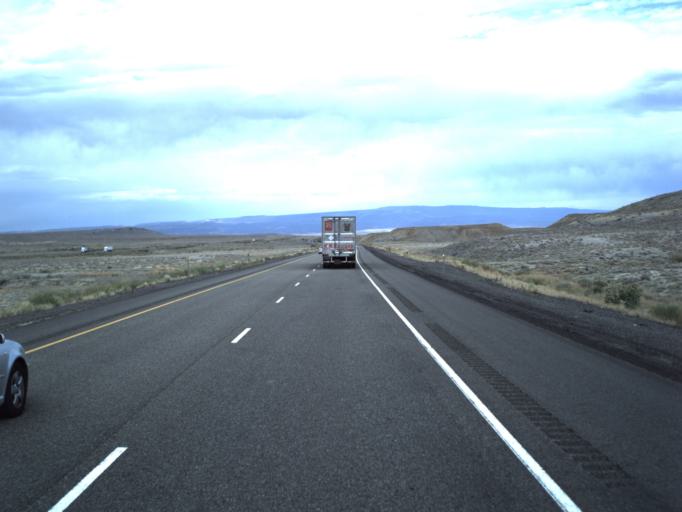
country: US
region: Utah
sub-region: Grand County
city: Moab
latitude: 38.9413
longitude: -109.5345
